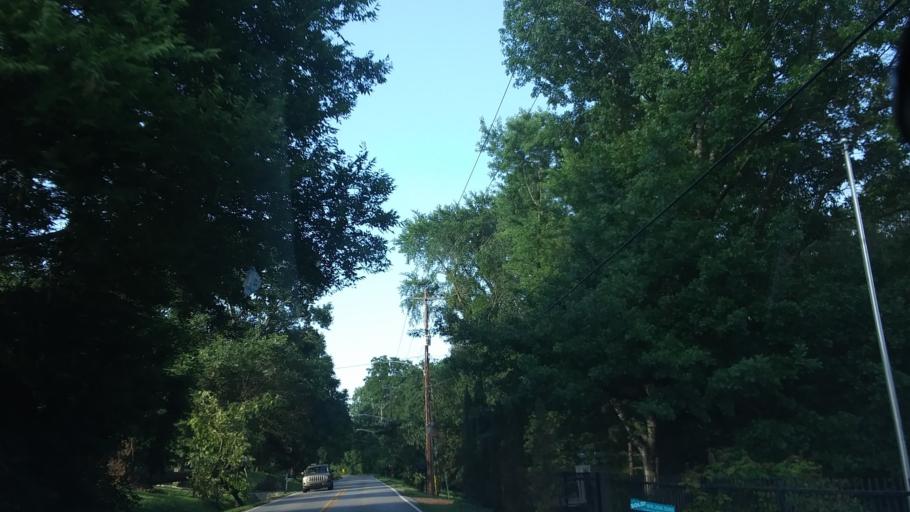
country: US
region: Tennessee
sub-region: Rutherford County
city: La Vergne
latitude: 36.0878
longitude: -86.6627
